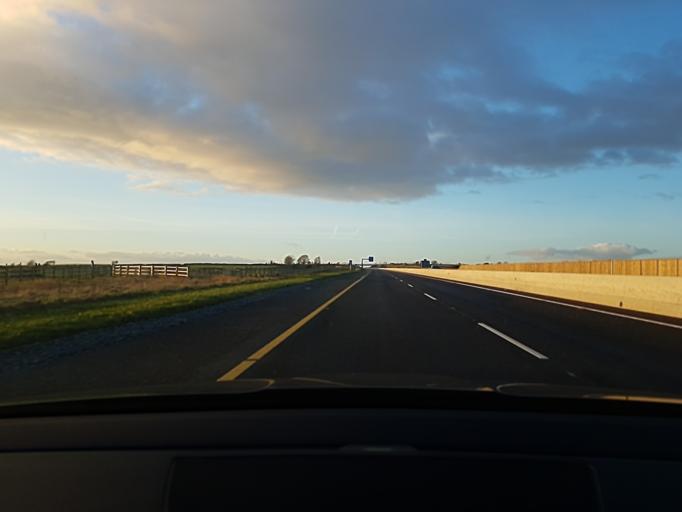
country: IE
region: Connaught
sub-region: County Galway
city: Athenry
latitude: 53.3967
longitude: -8.8078
